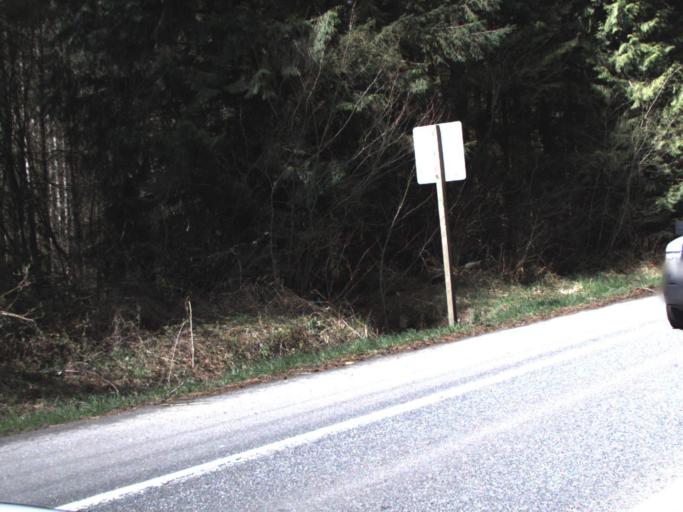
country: US
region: Washington
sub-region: King County
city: Black Diamond
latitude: 47.3302
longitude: -122.0103
